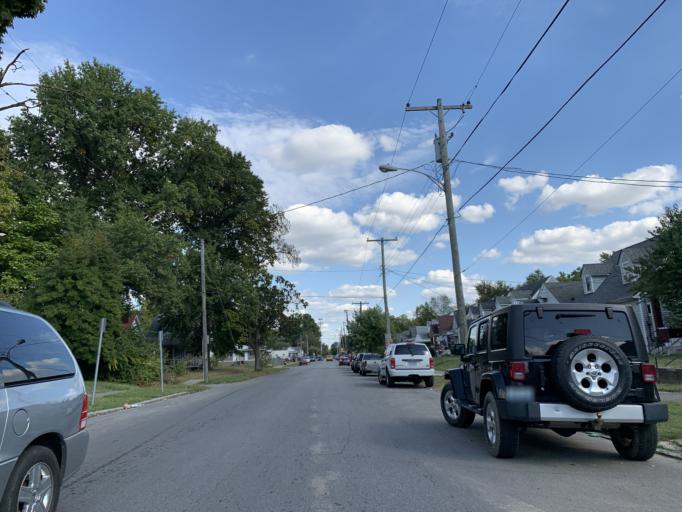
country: US
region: Indiana
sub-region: Floyd County
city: New Albany
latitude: 38.2458
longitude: -85.8086
